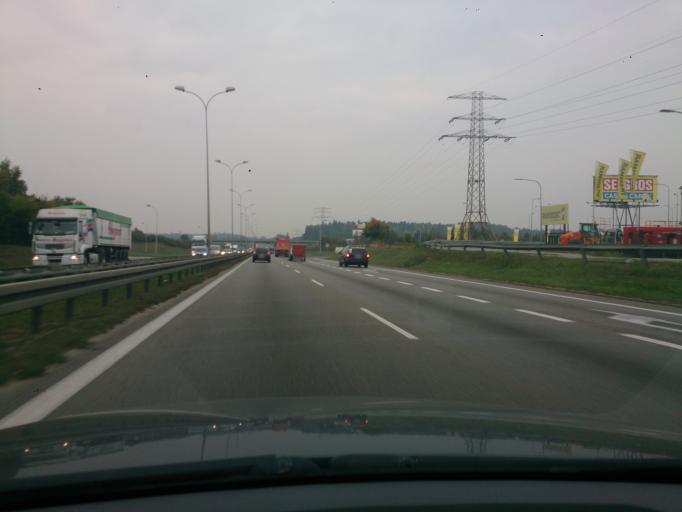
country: PL
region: Pomeranian Voivodeship
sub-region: Gdynia
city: Wielki Kack
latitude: 54.4158
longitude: 18.4866
